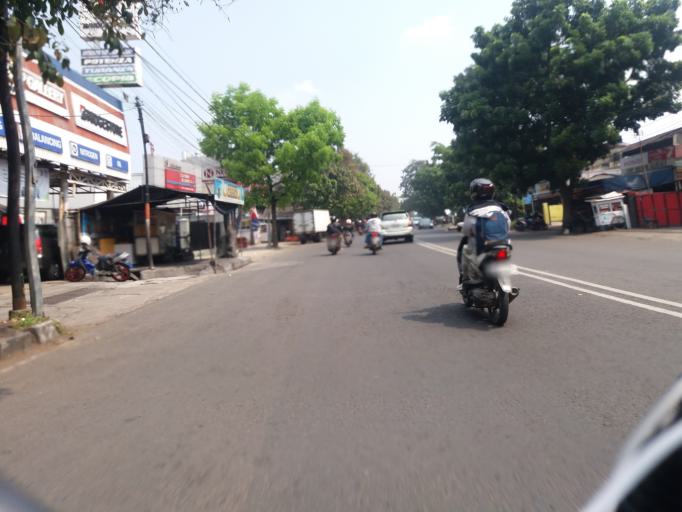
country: ID
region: West Java
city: Bandung
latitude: -6.9077
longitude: 107.5828
